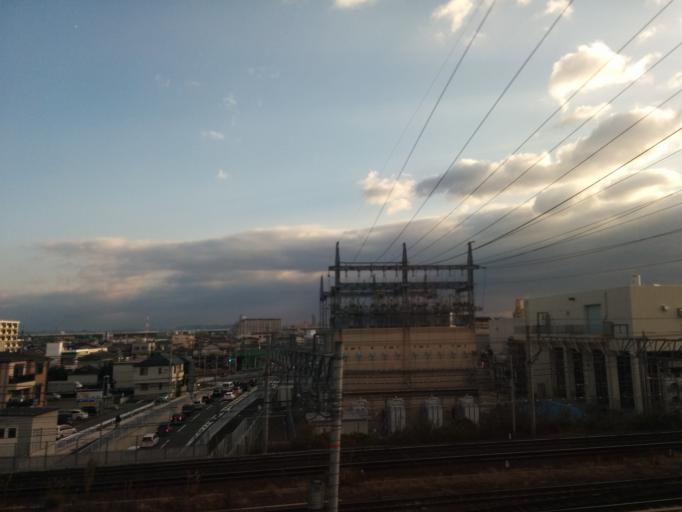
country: JP
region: Aichi
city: Nagoya-shi
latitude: 35.1979
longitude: 136.8623
